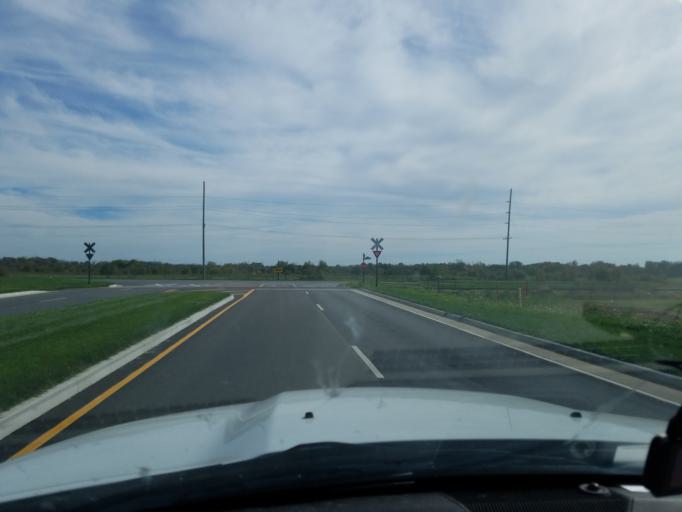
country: US
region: Kentucky
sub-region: Jefferson County
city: Prospect
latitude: 38.3821
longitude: -85.6662
